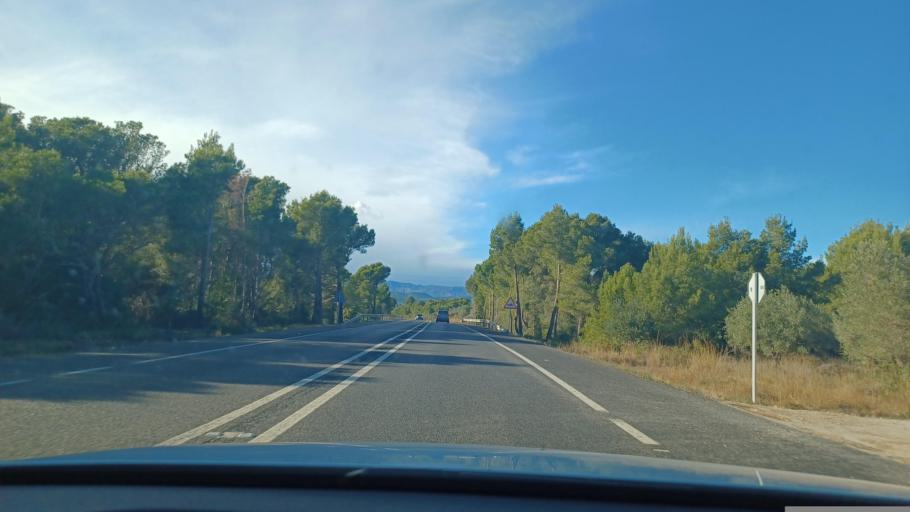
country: ES
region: Catalonia
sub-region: Provincia de Tarragona
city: l'Ametlla de Mar
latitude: 40.8945
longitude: 0.7721
